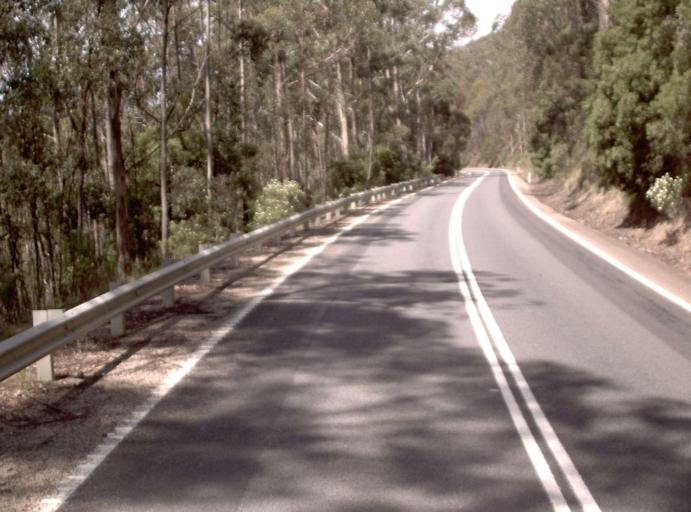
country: AU
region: New South Wales
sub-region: Bombala
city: Bombala
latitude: -37.5656
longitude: 149.3400
